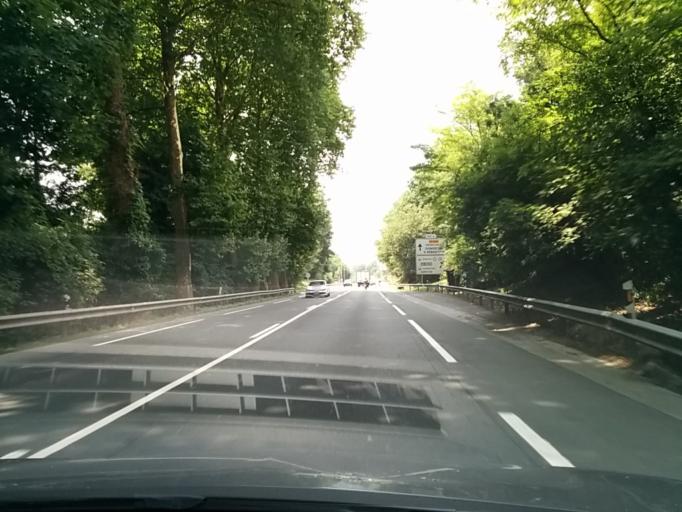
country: ES
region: Basque Country
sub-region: Provincia de Guipuzcoa
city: Lezo
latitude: 43.3229
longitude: -1.8631
